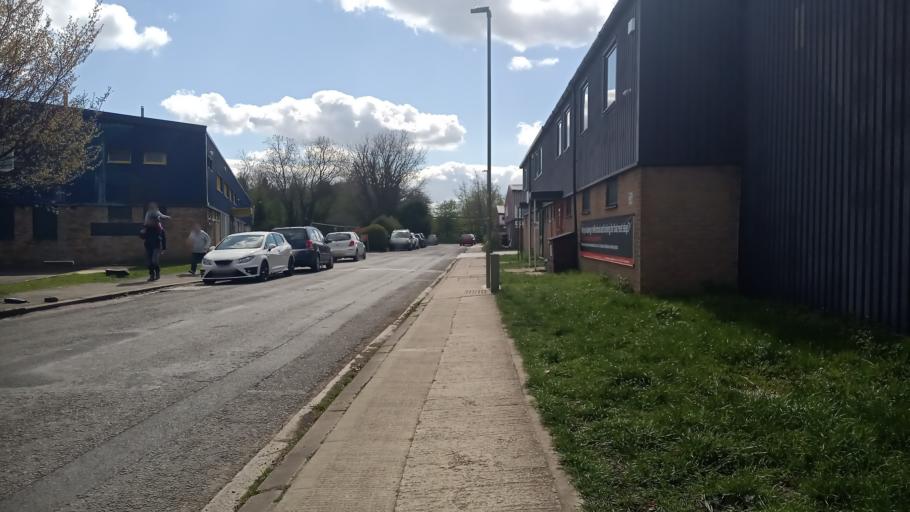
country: GB
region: England
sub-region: Oxfordshire
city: Witney
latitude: 51.7765
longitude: -1.4866
